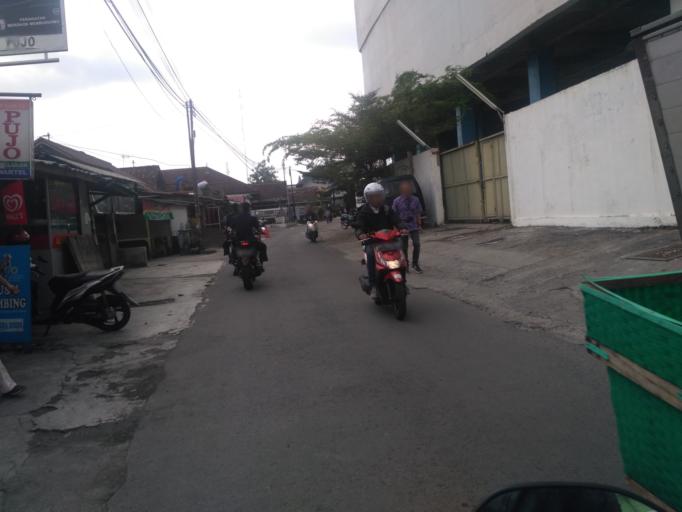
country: ID
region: Daerah Istimewa Yogyakarta
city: Melati
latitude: -7.7536
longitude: 110.3599
